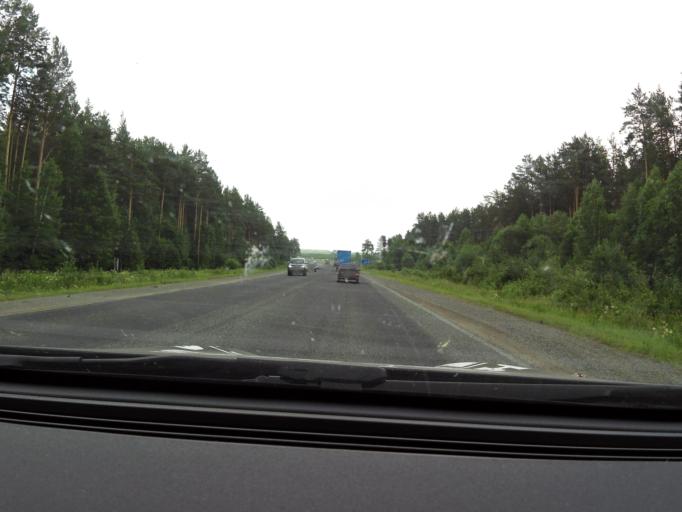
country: RU
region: Sverdlovsk
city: Ufimskiy
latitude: 56.7674
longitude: 58.1830
